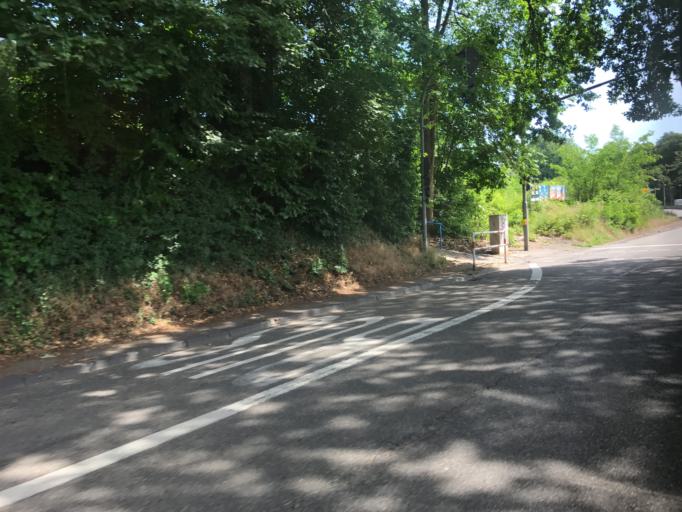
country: DE
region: Saarland
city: Saarbrucken
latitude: 49.2419
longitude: 7.0072
